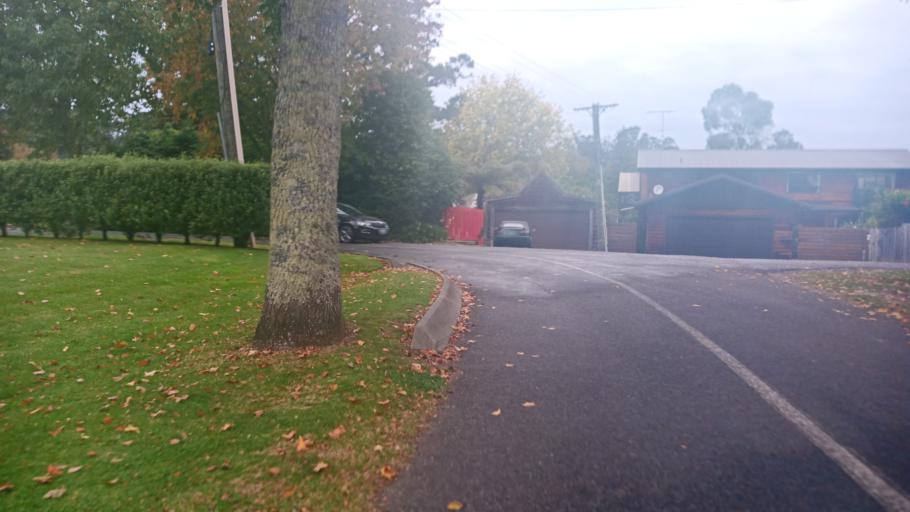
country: NZ
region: Gisborne
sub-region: Gisborne District
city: Gisborne
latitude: -38.6624
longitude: 178.0498
